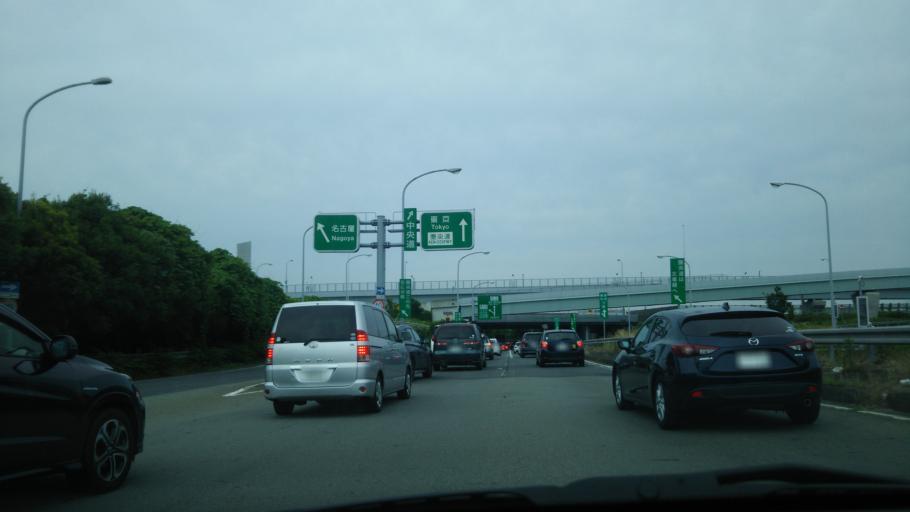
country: JP
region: Kanagawa
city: Atsugi
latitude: 35.4223
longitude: 139.3626
